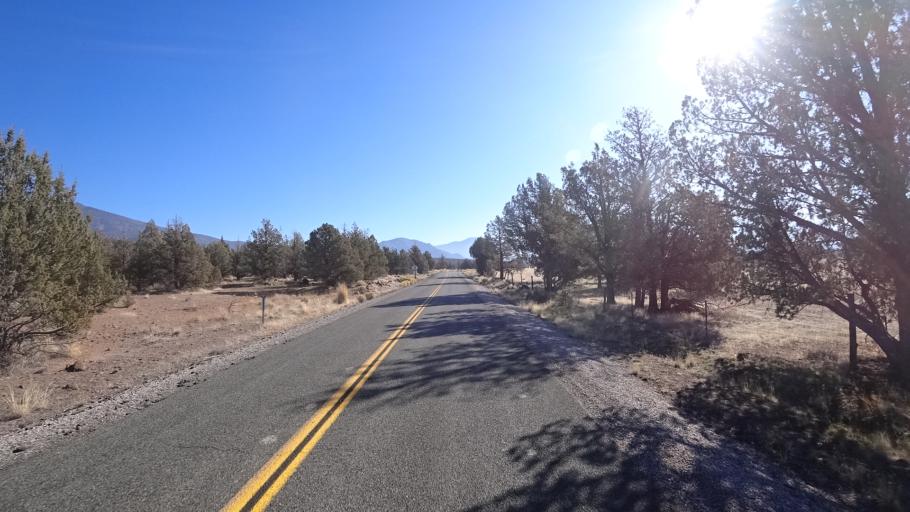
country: US
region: California
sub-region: Siskiyou County
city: Weed
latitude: 41.6025
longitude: -122.3046
